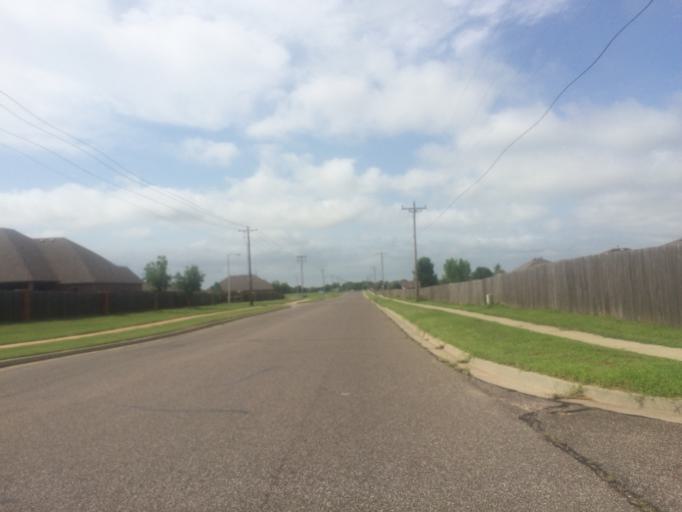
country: US
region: Oklahoma
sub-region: Cleveland County
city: Noble
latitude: 35.1692
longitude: -97.4237
